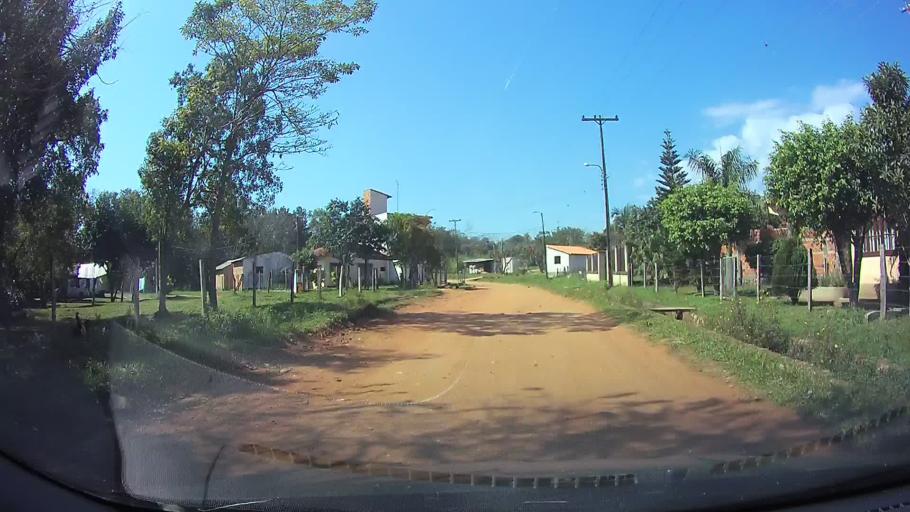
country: PY
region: Central
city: Limpio
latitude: -25.2296
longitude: -57.4413
